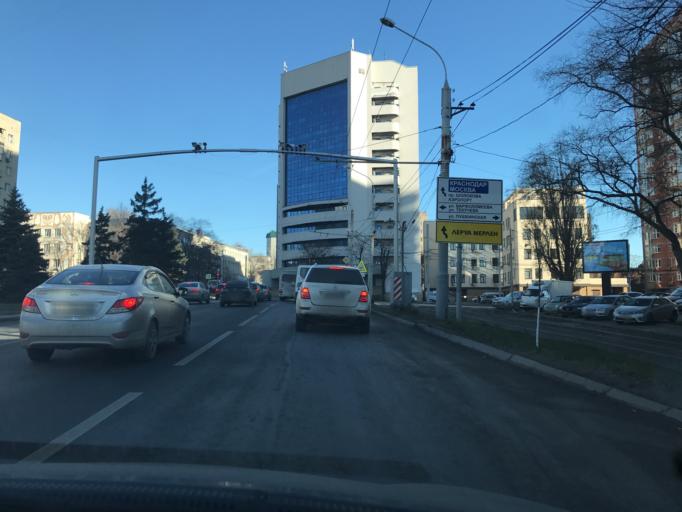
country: RU
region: Rostov
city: Rostov-na-Donu
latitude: 47.2237
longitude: 39.6949
